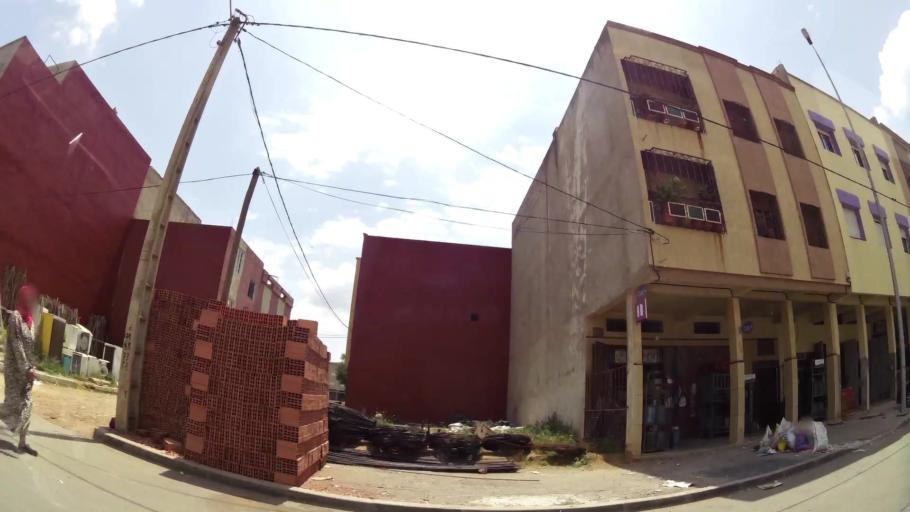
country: MA
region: Rabat-Sale-Zemmour-Zaer
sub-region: Khemisset
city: Tiflet
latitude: 34.0065
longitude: -6.5278
